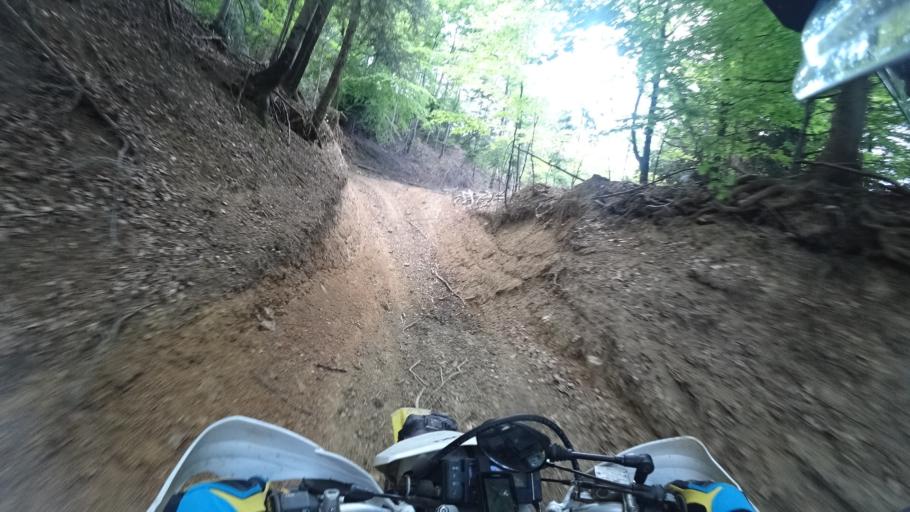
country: HR
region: Grad Zagreb
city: Kasina
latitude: 45.9268
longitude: 15.9518
